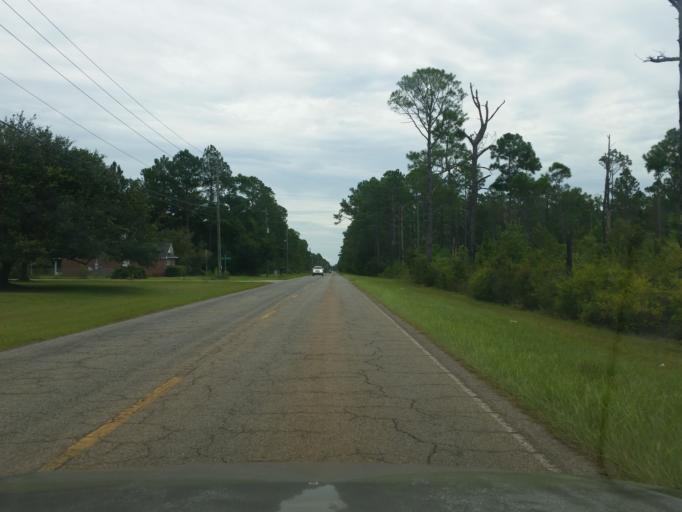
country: US
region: Florida
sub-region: Santa Rosa County
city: Pace
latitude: 30.5442
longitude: -87.1002
